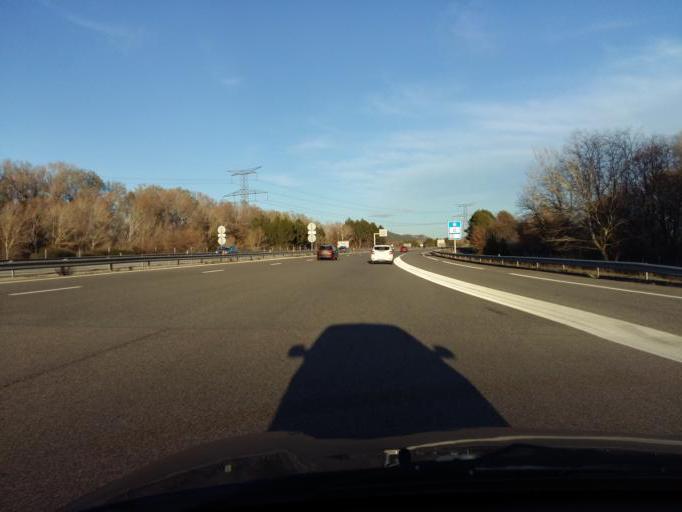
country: FR
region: Provence-Alpes-Cote d'Azur
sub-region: Departement des Bouches-du-Rhone
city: Meyrargues
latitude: 43.6617
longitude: 5.5066
